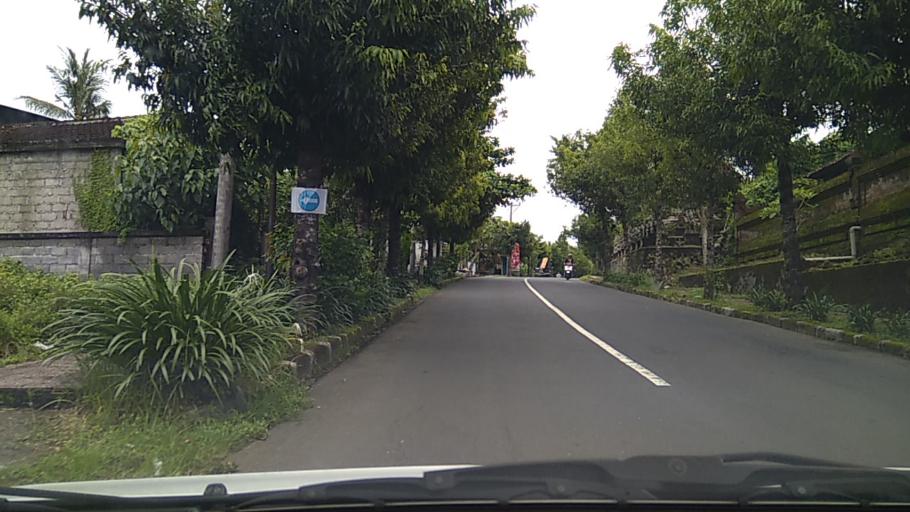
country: ID
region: Bali
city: Banjar Kelodan
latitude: -8.5304
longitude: 115.3483
